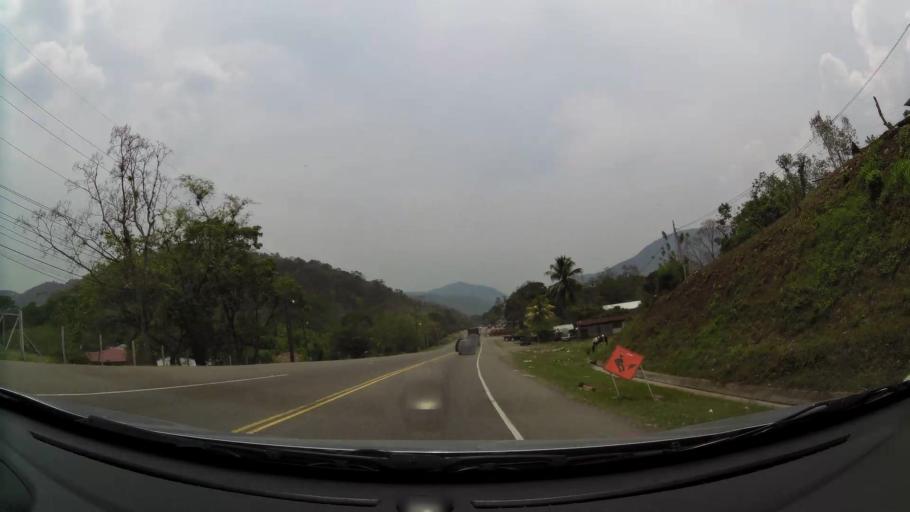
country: HN
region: Comayagua
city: Taulabe
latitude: 14.6981
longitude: -87.9630
